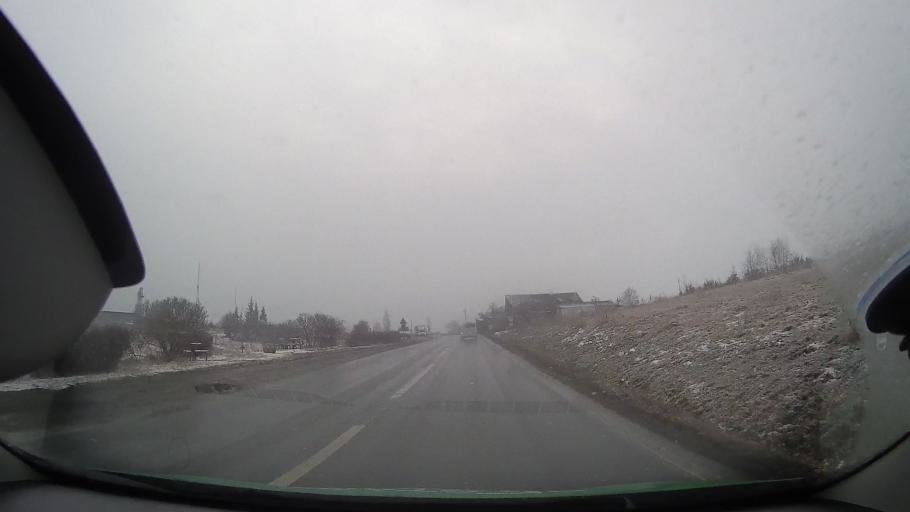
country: RO
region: Mures
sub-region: Comuna Bagaciu
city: Delenii
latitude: 46.2566
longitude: 24.2997
